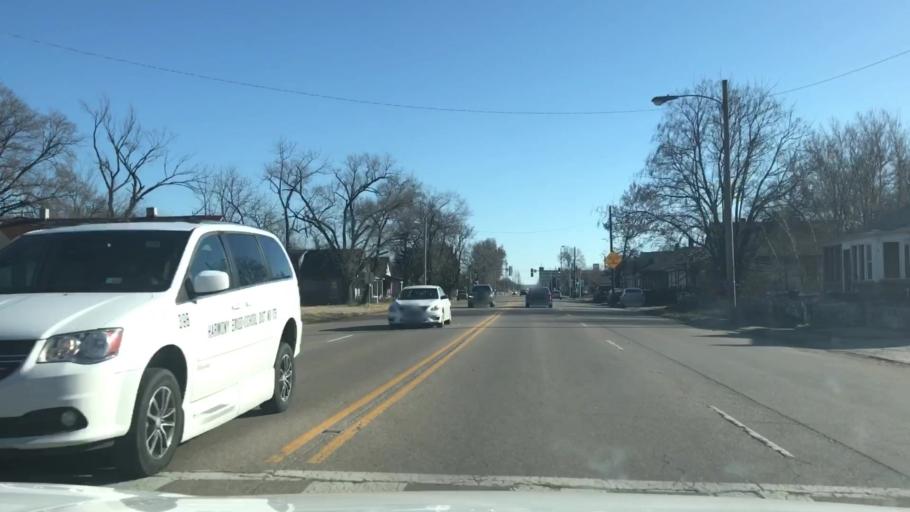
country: US
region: Illinois
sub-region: Saint Clair County
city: East Saint Louis
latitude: 38.6067
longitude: -90.1360
